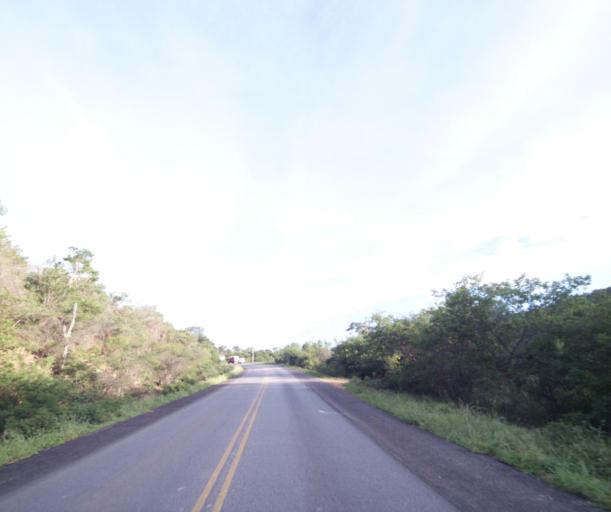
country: BR
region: Bahia
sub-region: Cacule
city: Cacule
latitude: -14.1966
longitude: -42.1402
